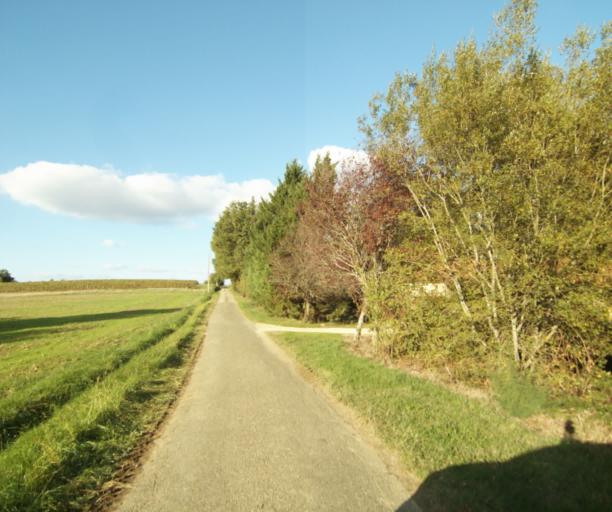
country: FR
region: Midi-Pyrenees
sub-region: Departement du Gers
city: Eauze
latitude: 43.7427
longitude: 0.1131
